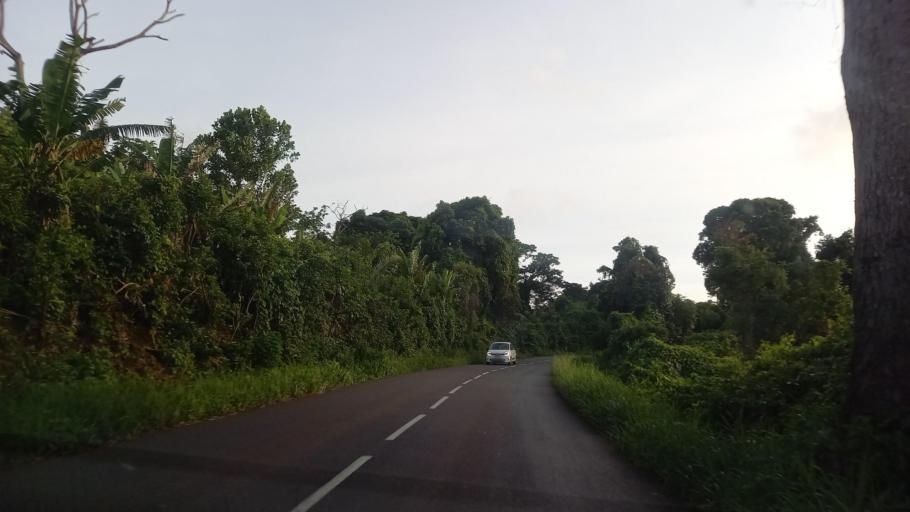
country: YT
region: Bandraboua
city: Bandraboua
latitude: -12.7410
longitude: 45.1173
